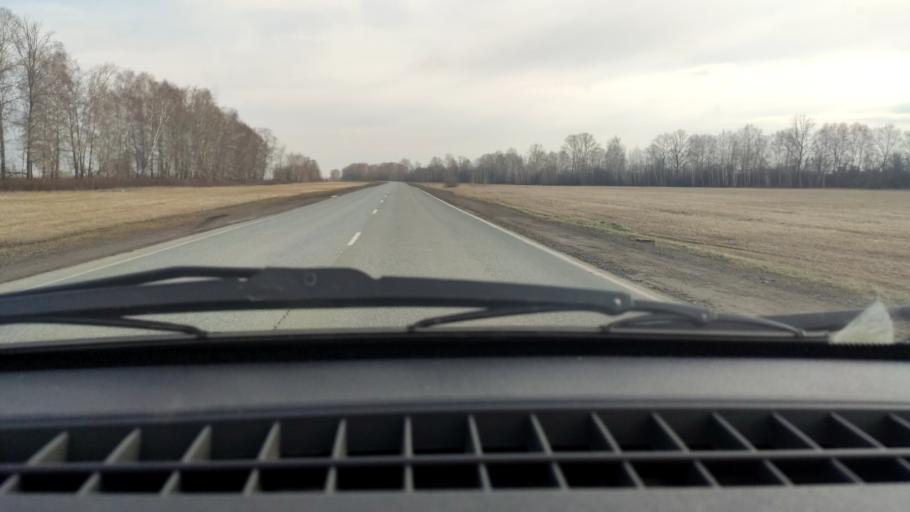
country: RU
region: Bashkortostan
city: Chishmy
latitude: 54.4057
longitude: 55.2180
